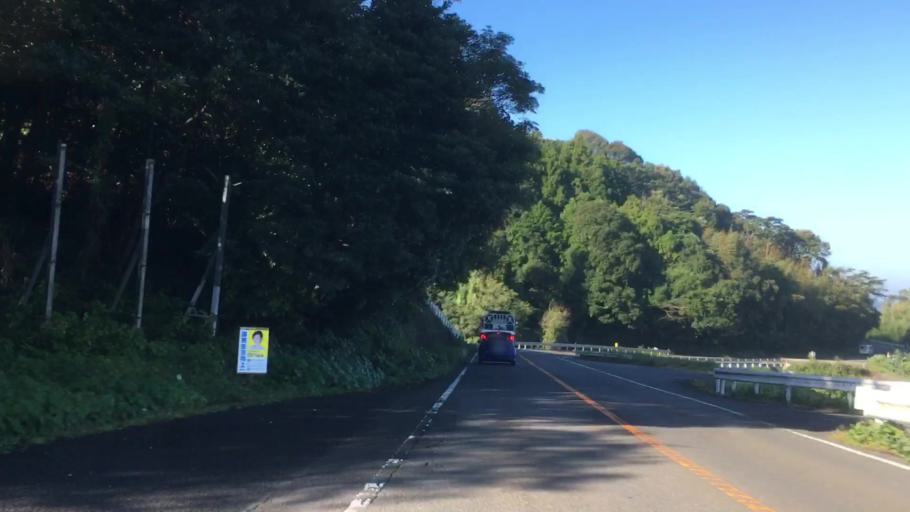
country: JP
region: Nagasaki
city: Sasebo
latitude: 33.0389
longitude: 129.6850
